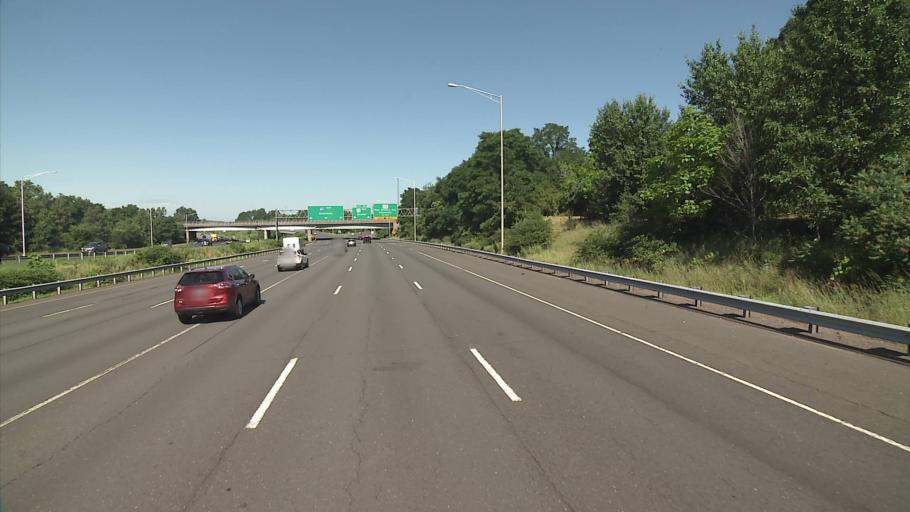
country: US
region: Connecticut
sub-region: Hartford County
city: Plainville
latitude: 41.6703
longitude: -72.8380
